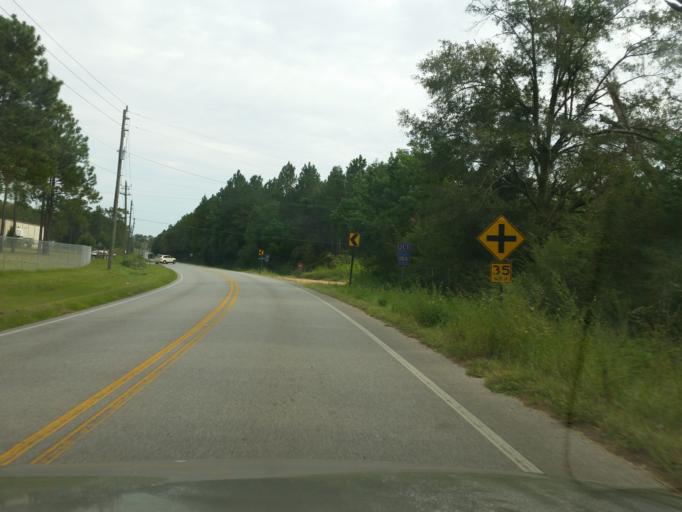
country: US
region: Florida
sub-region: Escambia County
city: Cantonment
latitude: 30.6515
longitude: -87.3219
